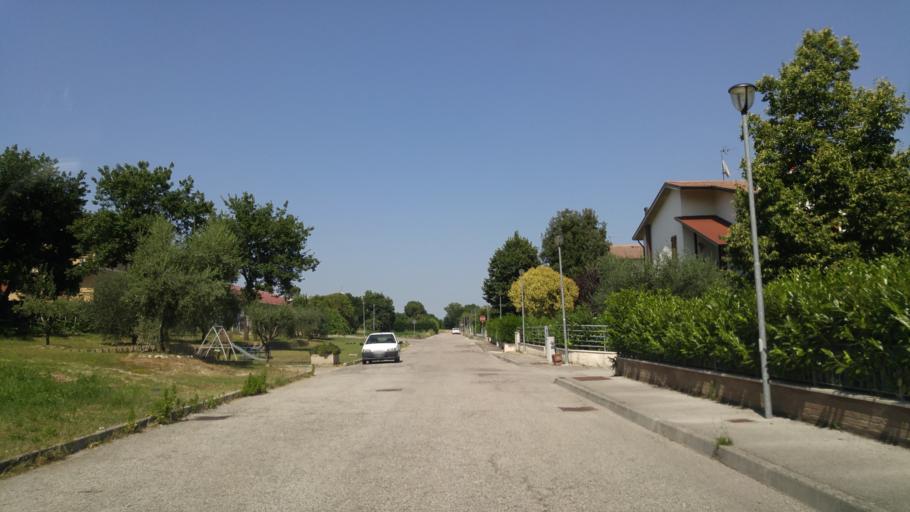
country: IT
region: The Marches
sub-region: Provincia di Pesaro e Urbino
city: Fossombrone
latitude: 43.6934
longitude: 12.8234
